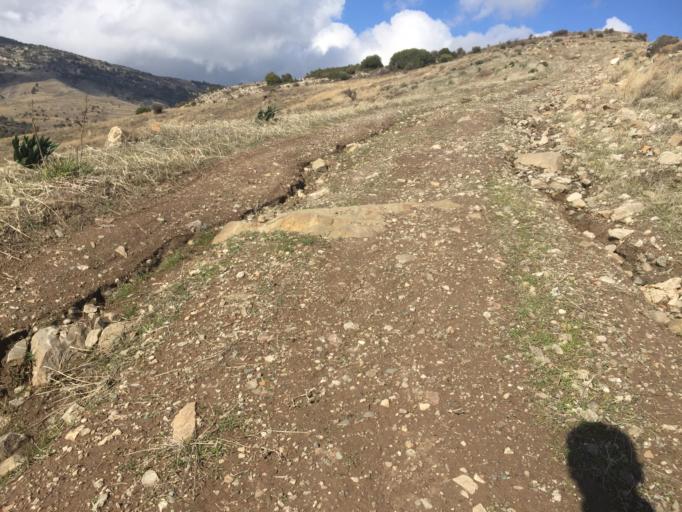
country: CY
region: Limassol
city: Pachna
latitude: 34.8770
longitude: 32.6547
